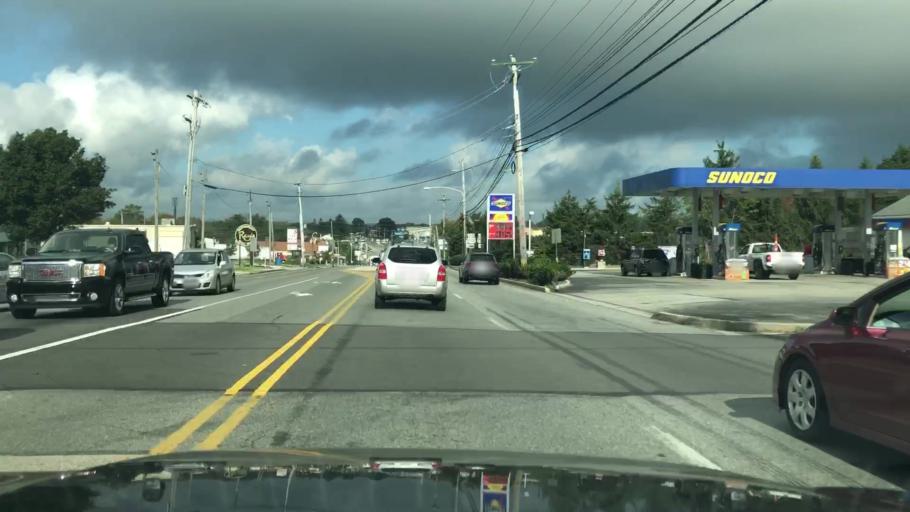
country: US
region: Pennsylvania
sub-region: Montgomery County
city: Norristown
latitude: 40.1405
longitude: -75.3108
